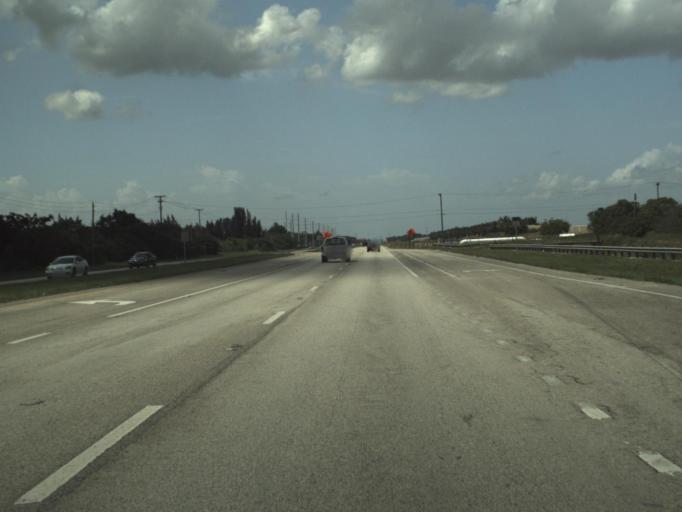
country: US
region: Florida
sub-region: Palm Beach County
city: Villages of Oriole
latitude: 26.4214
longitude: -80.2040
